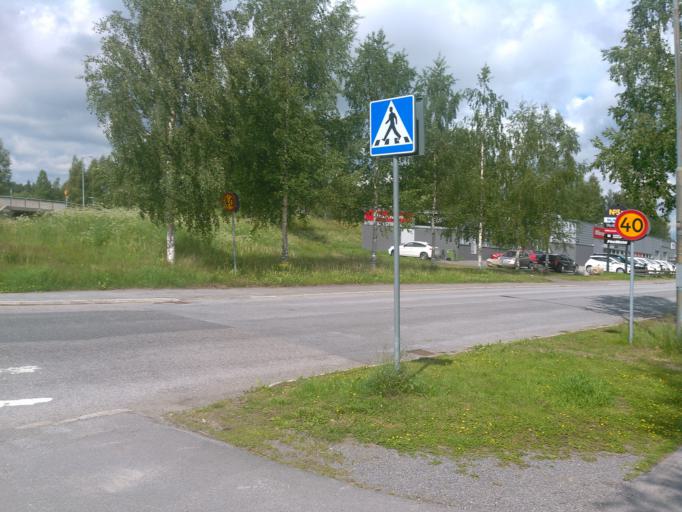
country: SE
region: Vaesterbotten
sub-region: Umea Kommun
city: Umea
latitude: 63.8365
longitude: 20.2725
